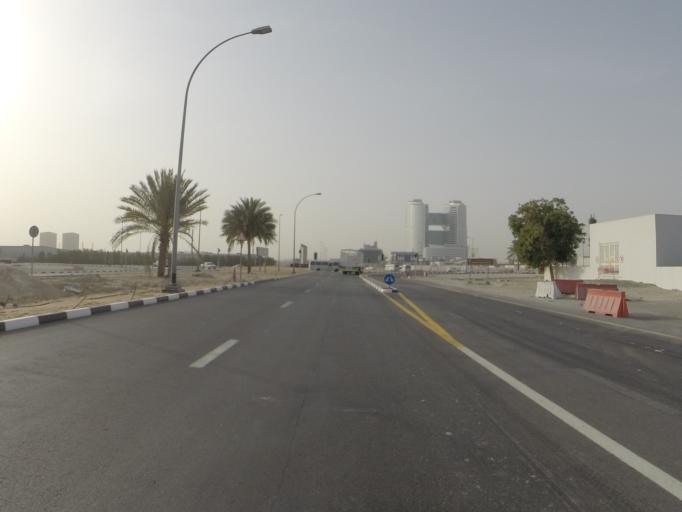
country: AE
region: Dubai
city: Dubai
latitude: 24.9716
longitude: 55.0758
